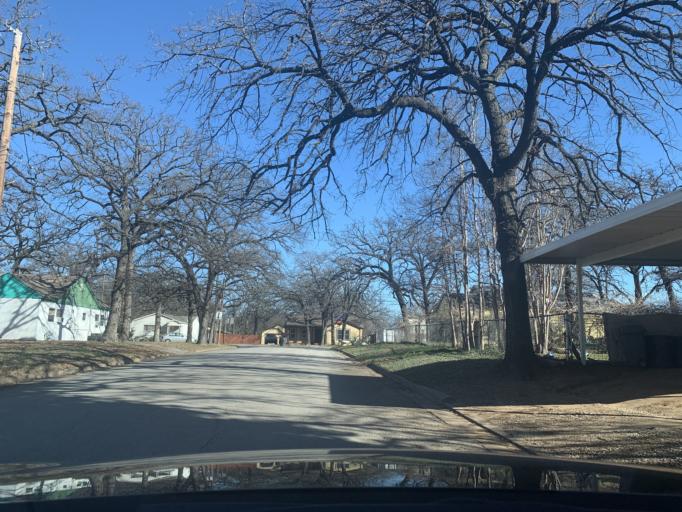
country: US
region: Texas
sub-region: Tarrant County
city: Haltom City
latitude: 32.7835
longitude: -97.2831
